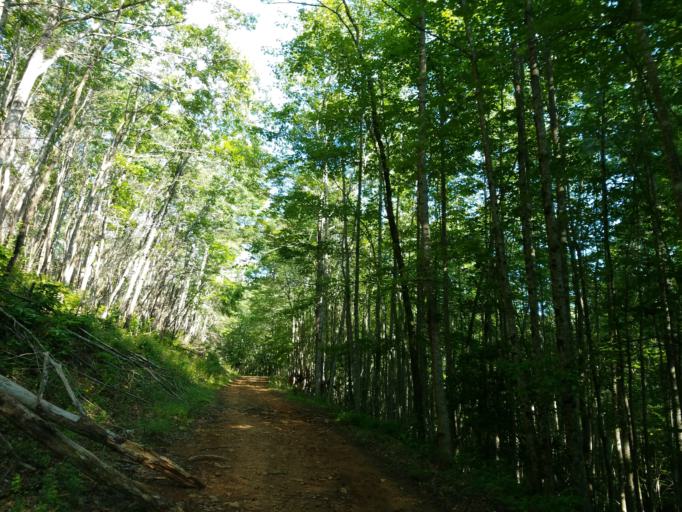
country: US
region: Georgia
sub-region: Fannin County
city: Blue Ridge
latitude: 34.7919
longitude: -84.2108
